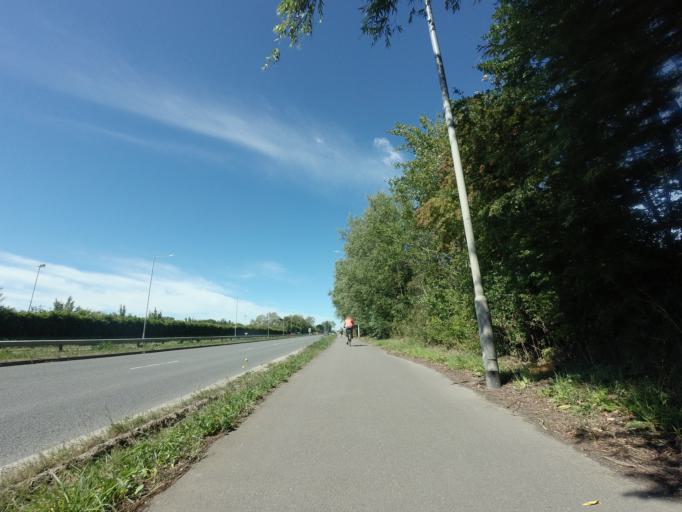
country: GB
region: England
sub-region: Kent
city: Sandwich
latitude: 51.2971
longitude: 1.3471
